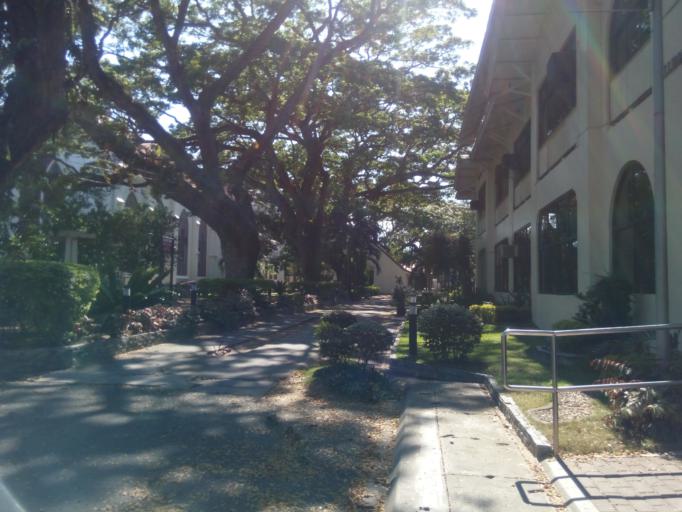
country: PH
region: Central Visayas
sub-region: Province of Negros Oriental
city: Dumaguete
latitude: 9.3112
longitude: 123.3060
